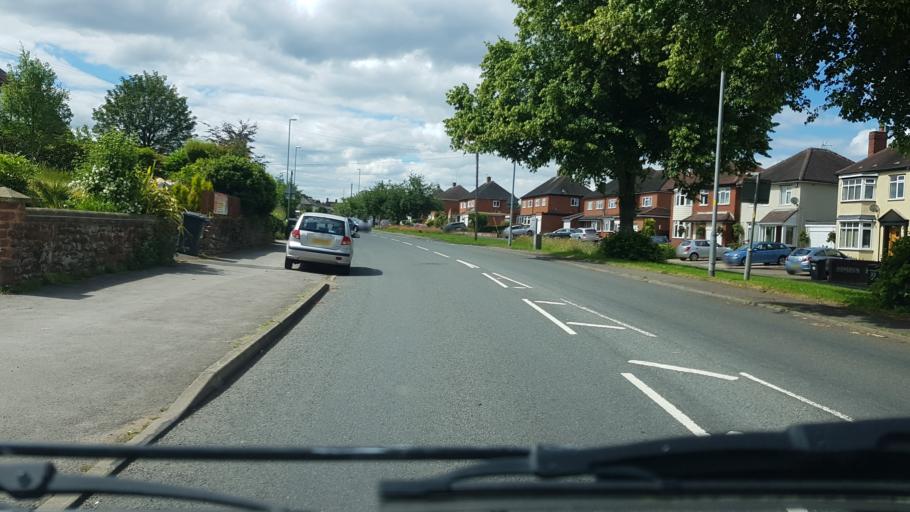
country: GB
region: England
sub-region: Worcestershire
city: Stourport-on-Severn
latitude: 52.3444
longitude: -2.2790
